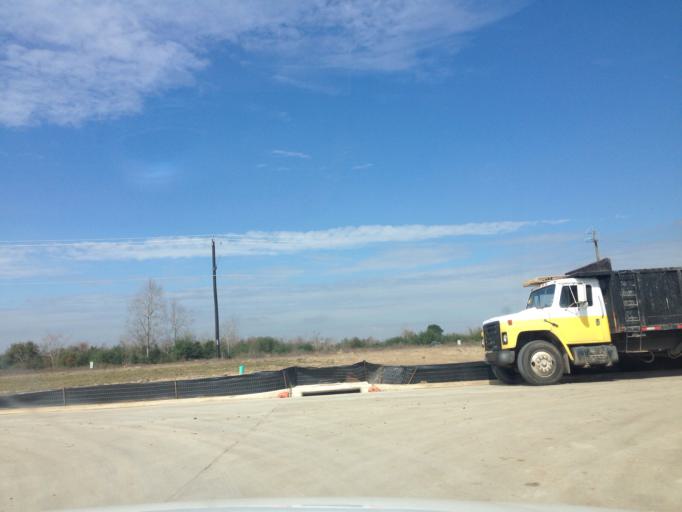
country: US
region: Texas
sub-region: Galveston County
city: Kemah
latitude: 29.5204
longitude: -95.0141
